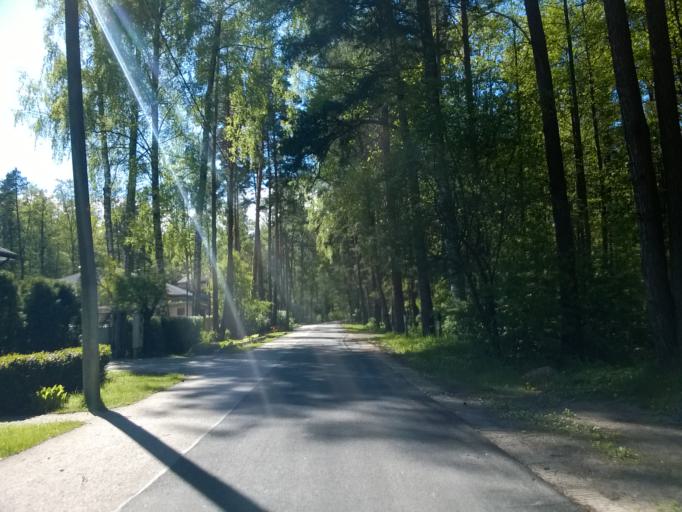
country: LV
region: Jurmala
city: Jurmala
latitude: 56.9589
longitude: 23.6549
